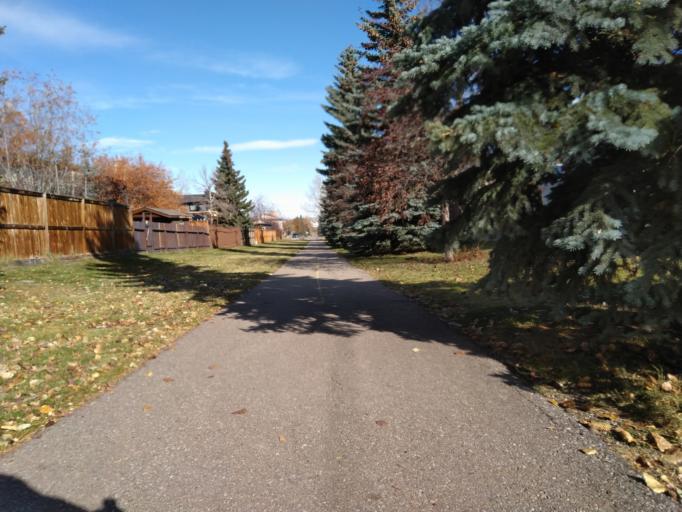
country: CA
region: Alberta
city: Calgary
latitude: 51.1260
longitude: -114.0860
